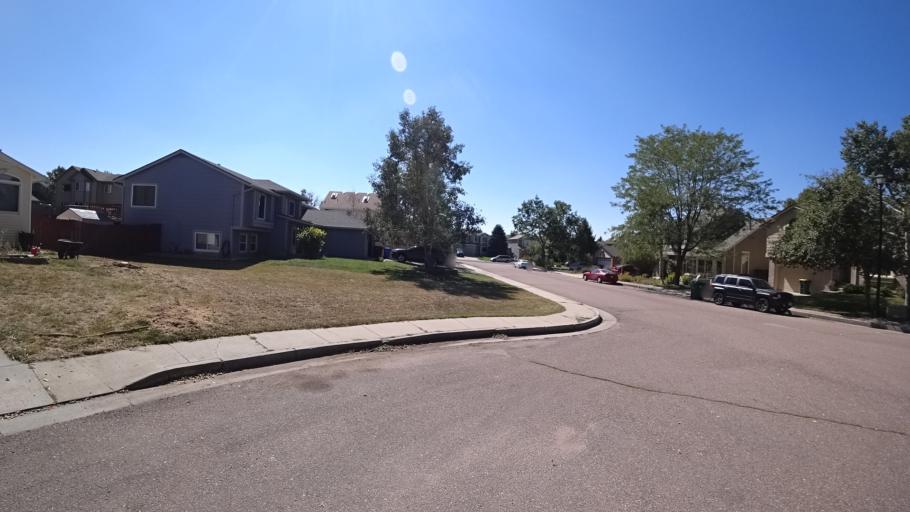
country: US
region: Colorado
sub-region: El Paso County
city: Cimarron Hills
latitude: 38.8982
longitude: -104.7013
